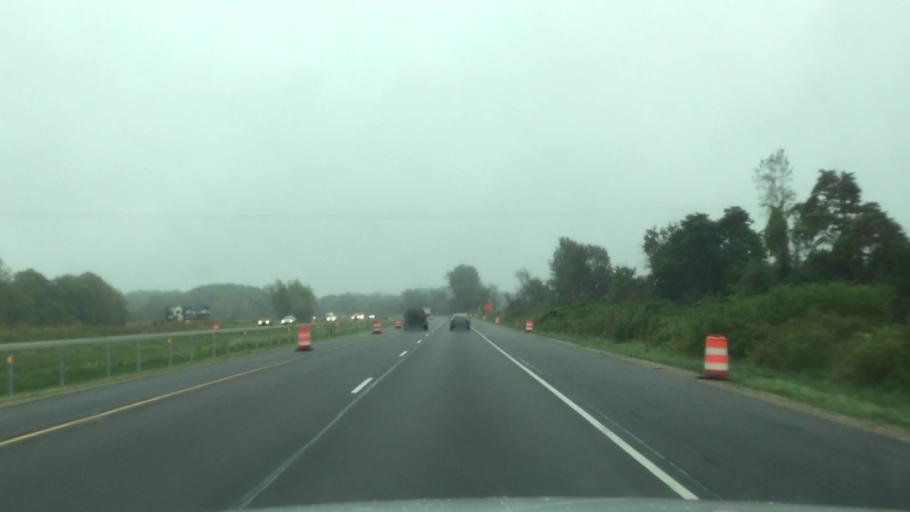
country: US
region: Michigan
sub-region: Van Buren County
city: Decatur
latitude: 42.1912
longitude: -86.0118
